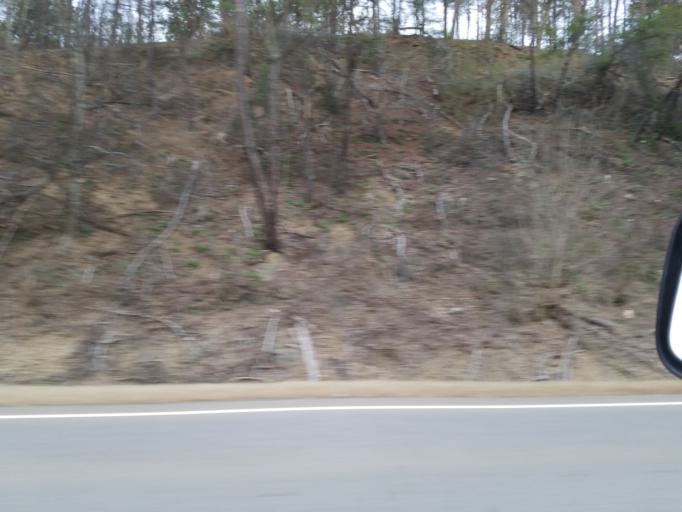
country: US
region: Georgia
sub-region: Bartow County
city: Rydal
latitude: 34.4504
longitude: -84.7569
